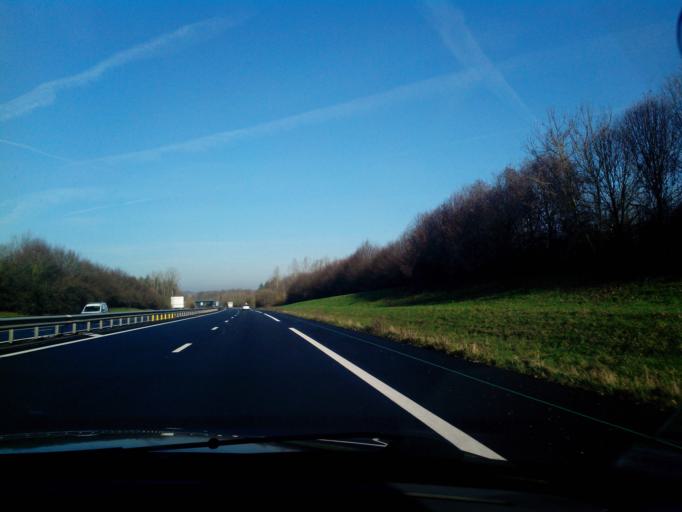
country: FR
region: Picardie
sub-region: Departement de l'Oise
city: Saint-Sulpice
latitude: 49.3473
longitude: 2.1078
